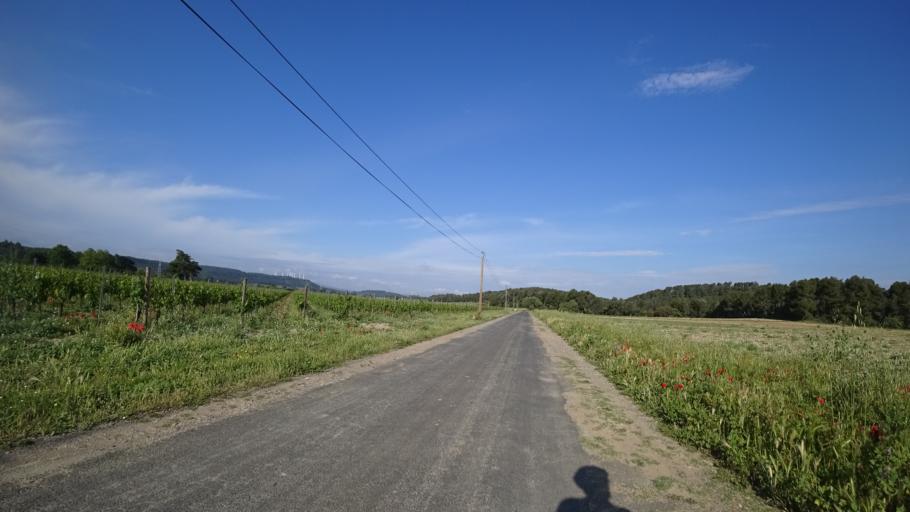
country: FR
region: Languedoc-Roussillon
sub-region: Departement de l'Aude
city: Lezignan-Corbieres
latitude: 43.2361
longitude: 2.7567
